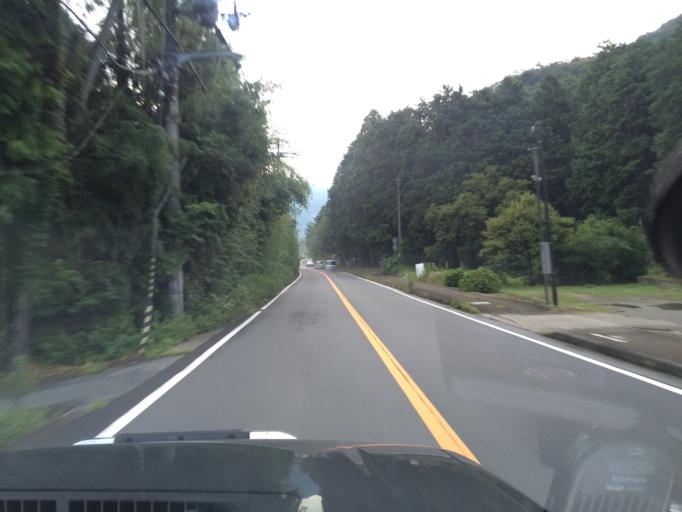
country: JP
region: Hyogo
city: Nishiwaki
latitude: 35.0935
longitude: 134.9979
